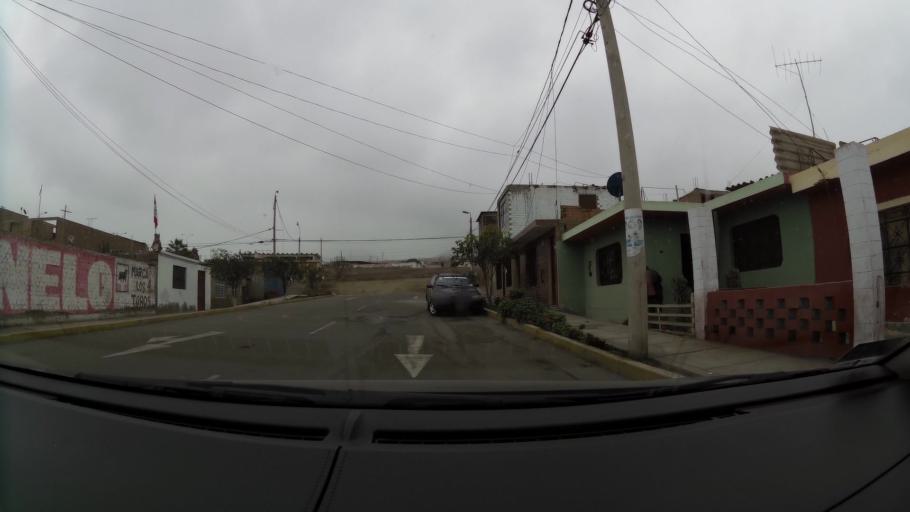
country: PE
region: Lima
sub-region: Provincia de Huaral
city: Chancay
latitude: -11.5905
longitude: -77.2595
